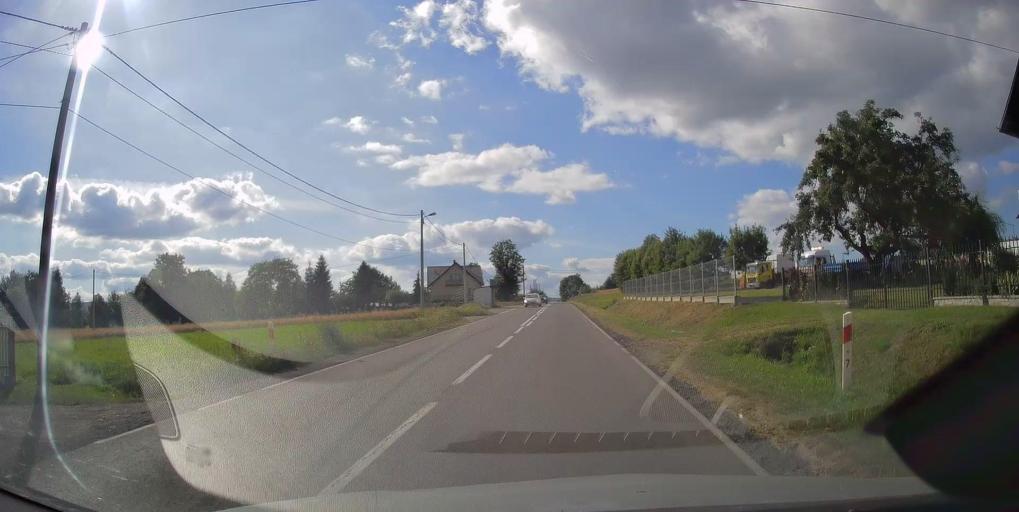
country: PL
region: Swietokrzyskie
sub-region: Powiat kielecki
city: Bodzentyn
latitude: 50.9699
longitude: 20.8833
